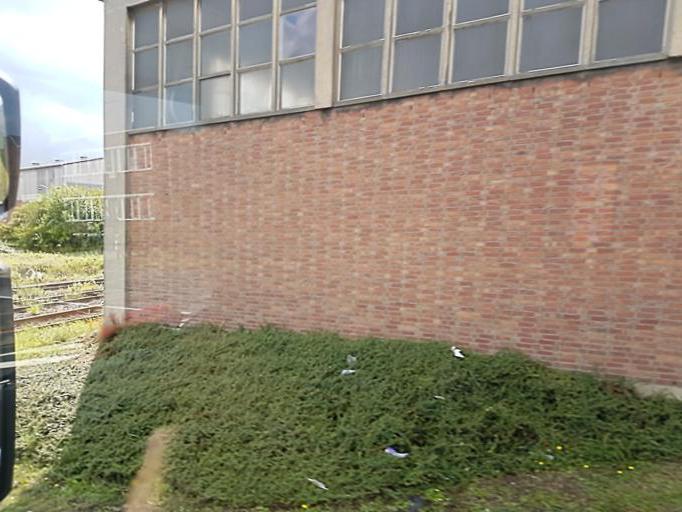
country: BE
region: Flanders
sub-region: Provincie Antwerpen
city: Antwerpen
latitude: 51.2550
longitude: 4.3885
